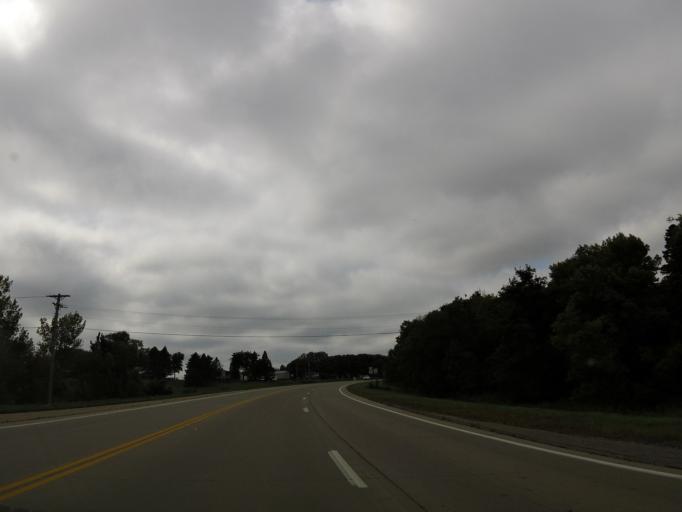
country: US
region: Minnesota
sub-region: Chippewa County
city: Montevideo
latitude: 44.9323
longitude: -95.7338
